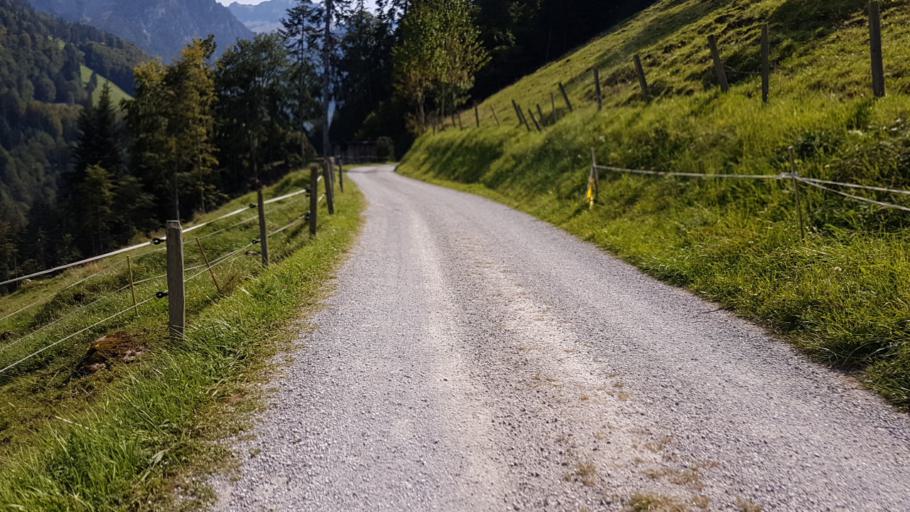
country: CH
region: Bern
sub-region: Frutigen-Niedersimmental District
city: Frutigen
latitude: 46.6024
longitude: 7.6975
